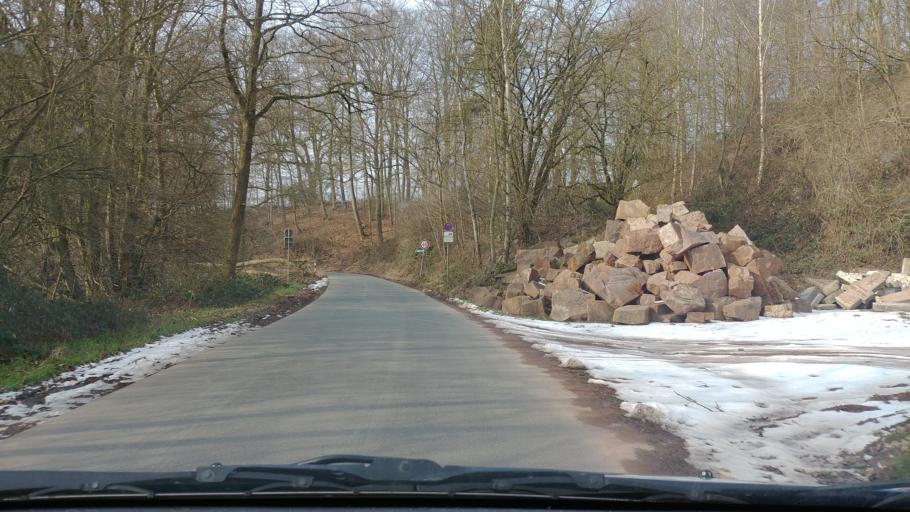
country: DE
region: Lower Saxony
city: Bad Karlshafen
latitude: 51.6512
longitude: 9.4388
